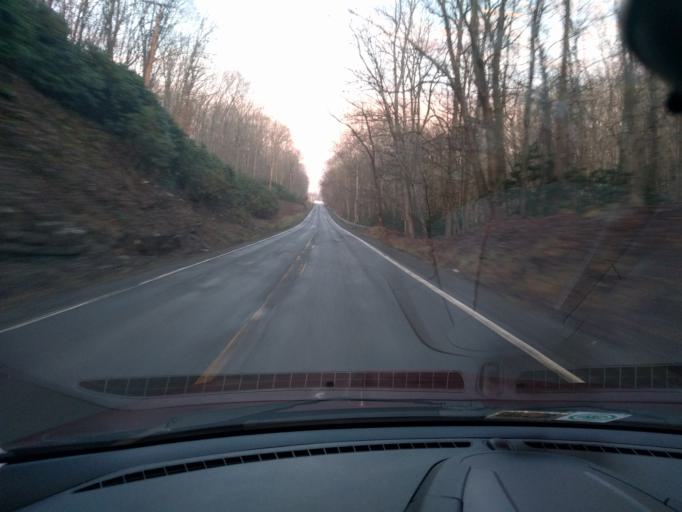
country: US
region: West Virginia
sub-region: Fayette County
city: Fayetteville
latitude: 38.0491
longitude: -80.9443
